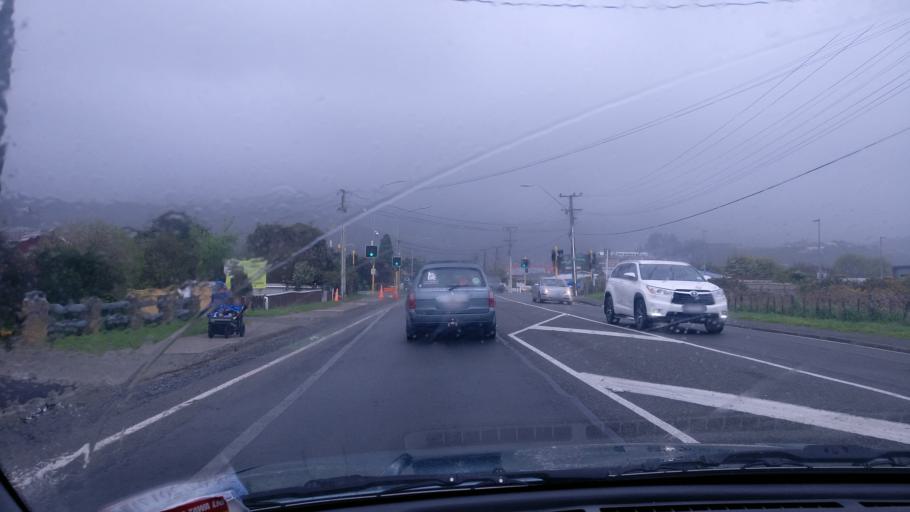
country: NZ
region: Wellington
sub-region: Kapiti Coast District
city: Paraparaumu
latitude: -40.9110
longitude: 175.0024
